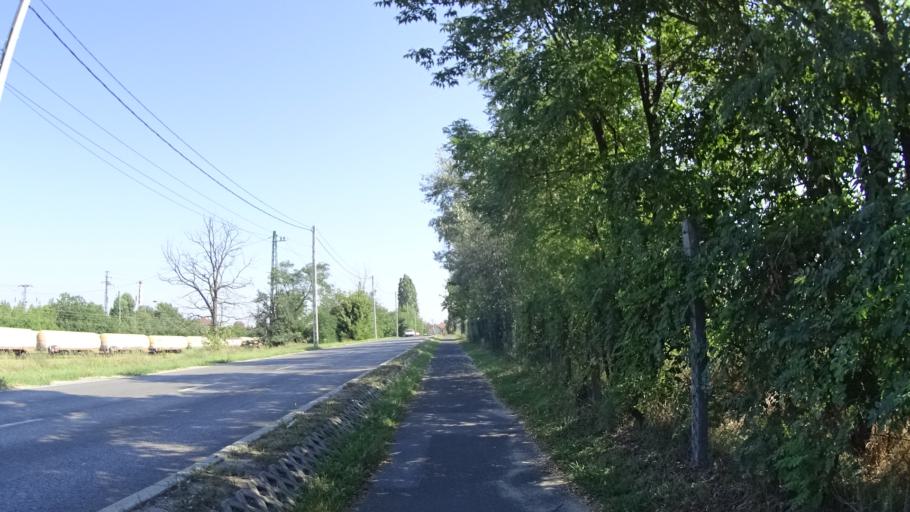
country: HU
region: Pest
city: Dunakeszi
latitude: 47.6219
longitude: 19.1351
